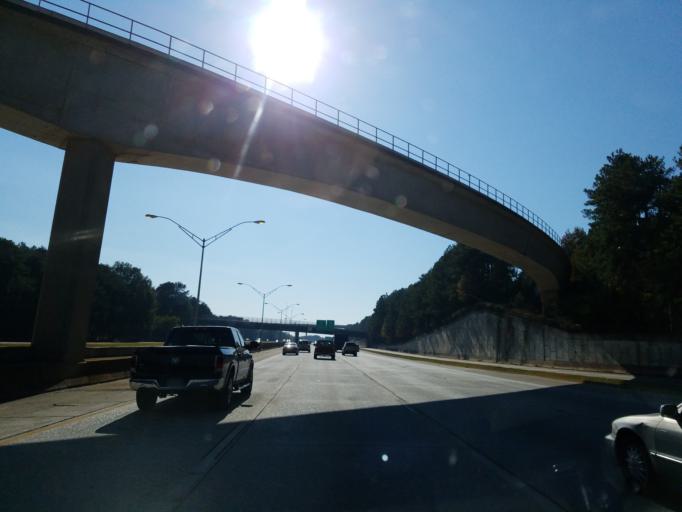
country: US
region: Georgia
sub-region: Fulton County
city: College Park
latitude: 33.6470
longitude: -84.4482
